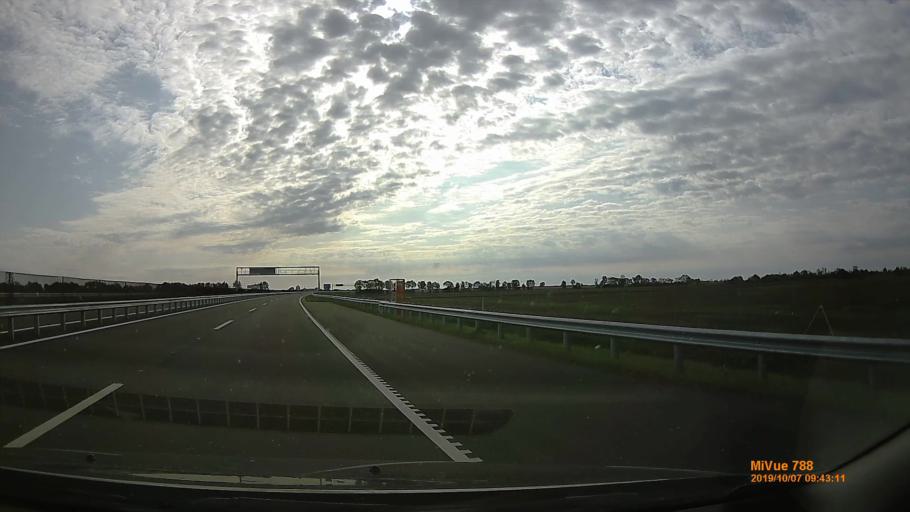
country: HU
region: Bekes
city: Kondoros
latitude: 46.8091
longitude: 20.6850
